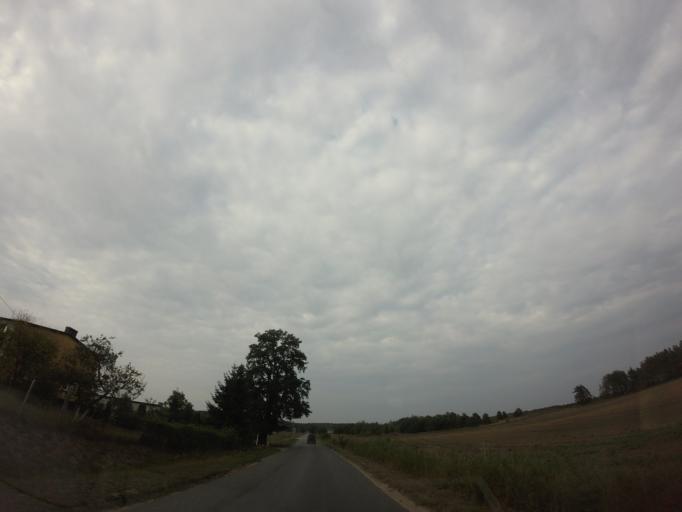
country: PL
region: West Pomeranian Voivodeship
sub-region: Powiat drawski
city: Drawsko Pomorskie
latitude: 53.4965
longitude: 15.7825
